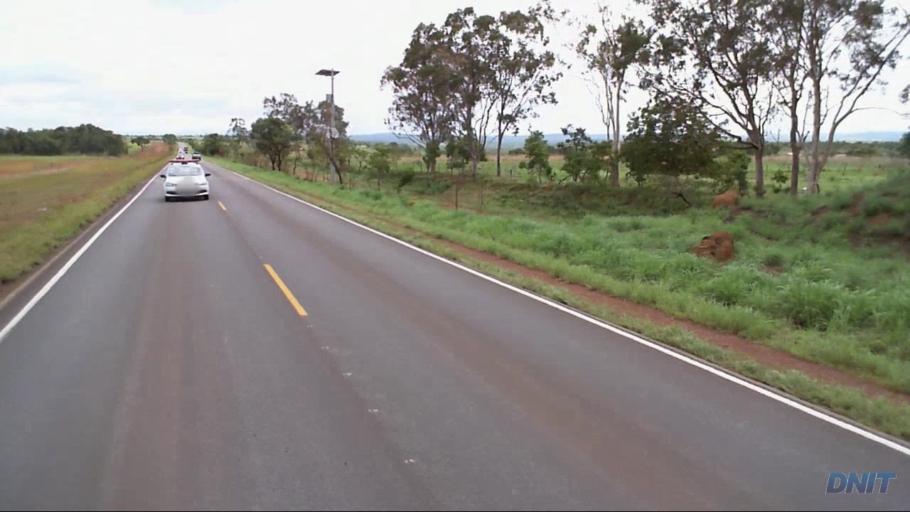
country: BR
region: Goias
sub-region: Padre Bernardo
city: Padre Bernardo
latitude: -15.3179
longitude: -48.2291
